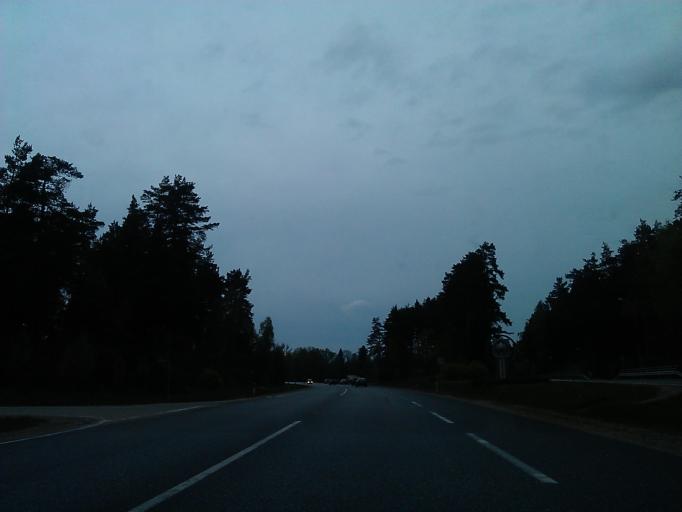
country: LV
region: Adazi
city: Adazi
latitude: 57.0588
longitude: 24.3220
